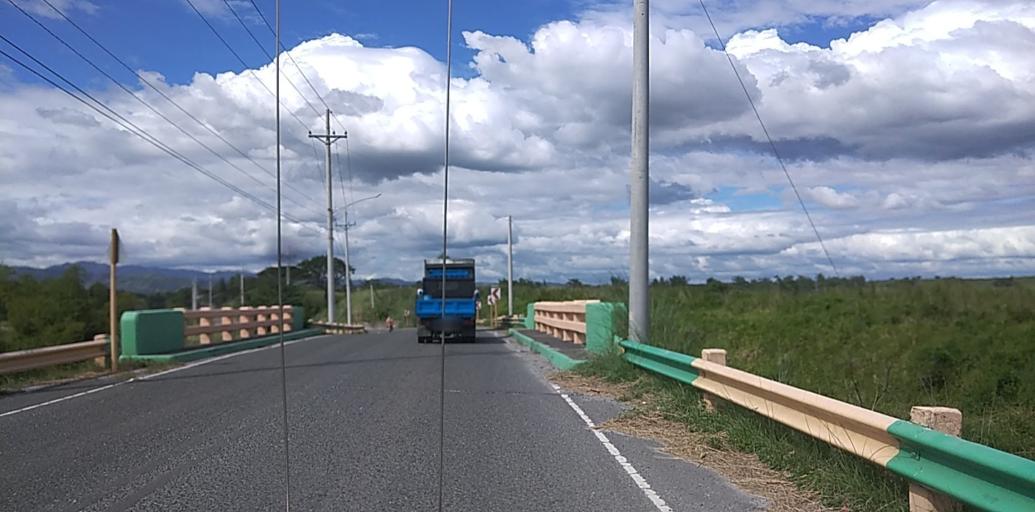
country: PH
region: Central Luzon
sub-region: Province of Pampanga
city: Dolores
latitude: 15.0876
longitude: 120.5394
